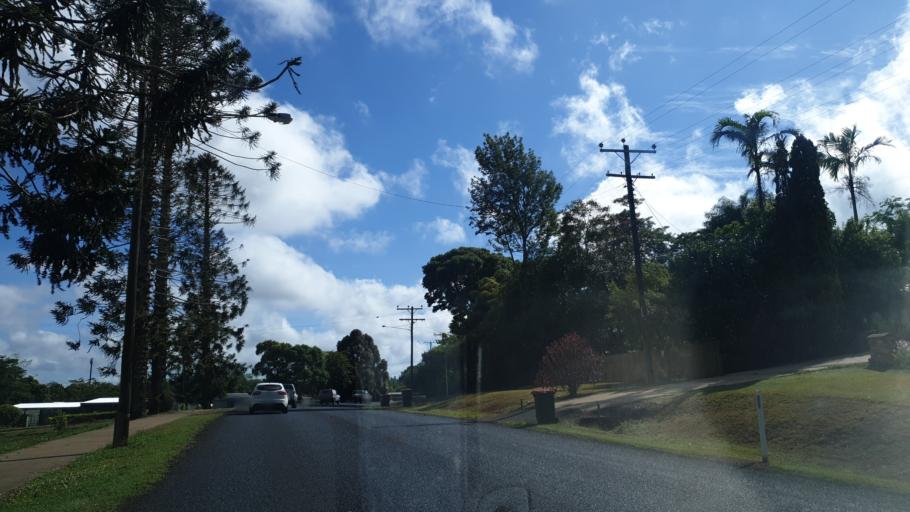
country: AU
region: Queensland
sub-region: Tablelands
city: Atherton
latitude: -17.3530
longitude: 145.5889
